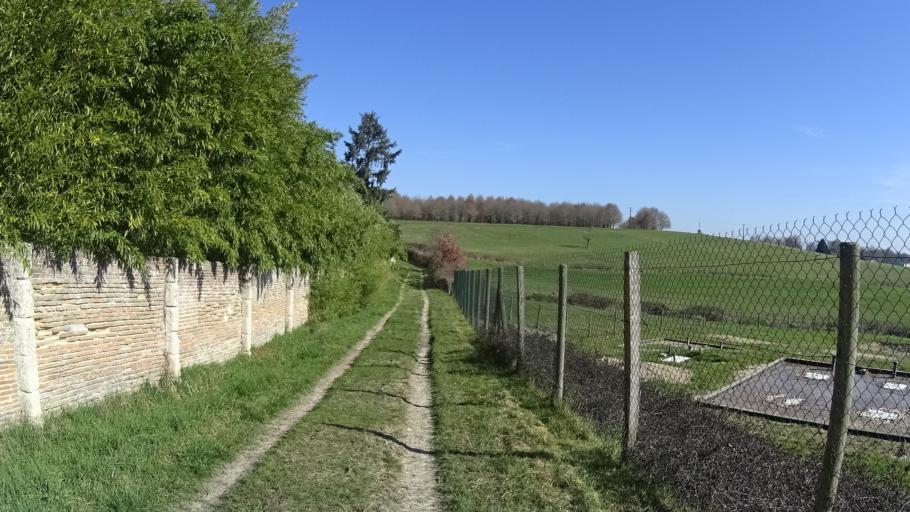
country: FR
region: Aquitaine
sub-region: Departement de la Dordogne
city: Saint-Aulaye
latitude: 45.1272
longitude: 0.2143
